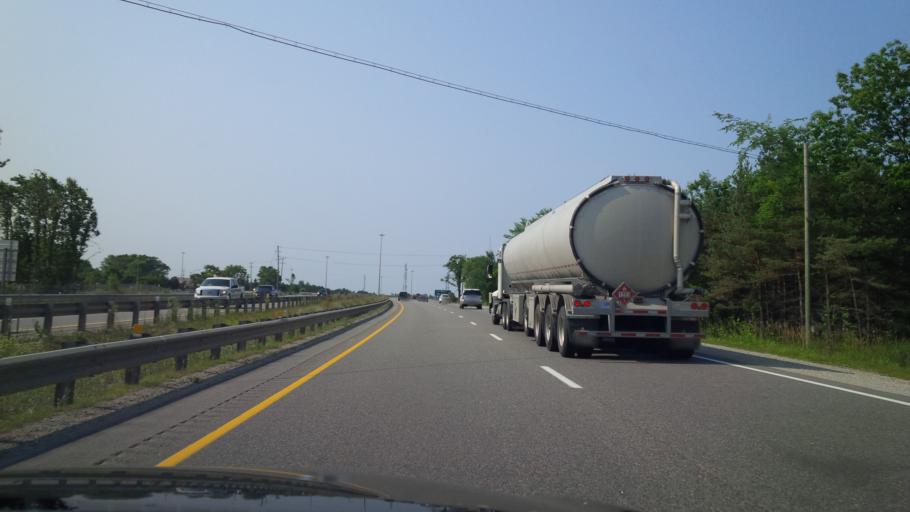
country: CA
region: Ontario
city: Orillia
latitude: 44.6170
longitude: -79.4435
